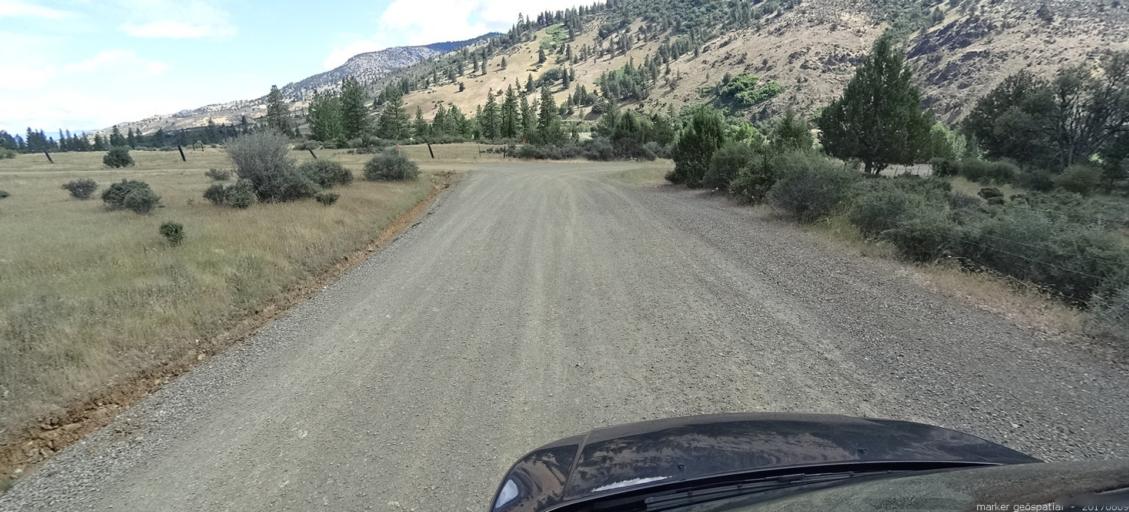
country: US
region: California
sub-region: Siskiyou County
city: Weed
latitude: 41.3215
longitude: -122.8144
